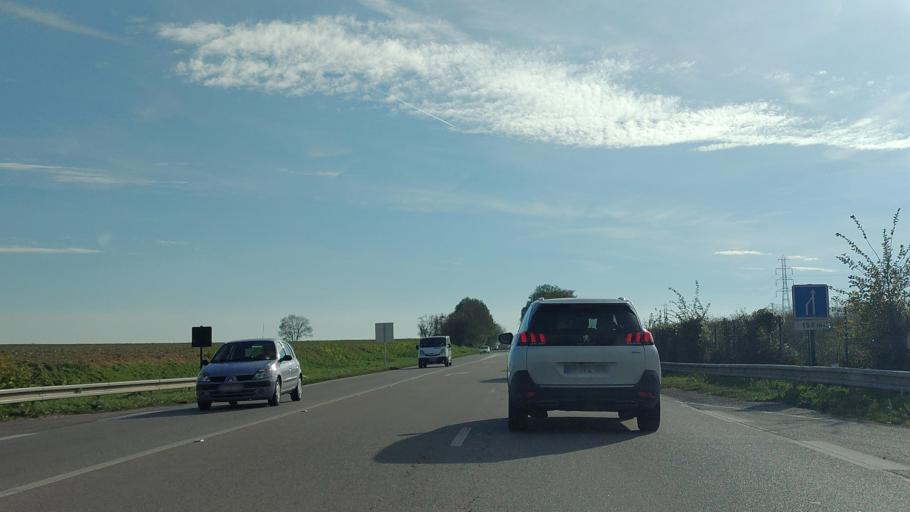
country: FR
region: Ile-de-France
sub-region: Departement du Val-d'Oise
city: Survilliers
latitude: 49.0831
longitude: 2.5297
